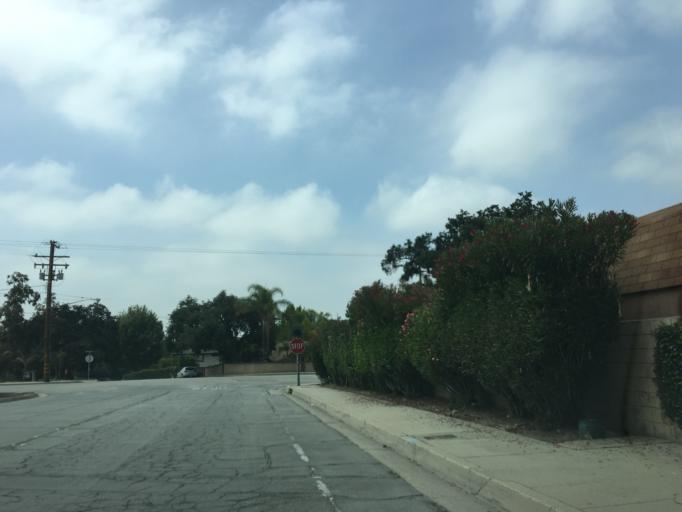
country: US
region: California
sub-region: Los Angeles County
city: Glendora
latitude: 34.1475
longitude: -117.8380
